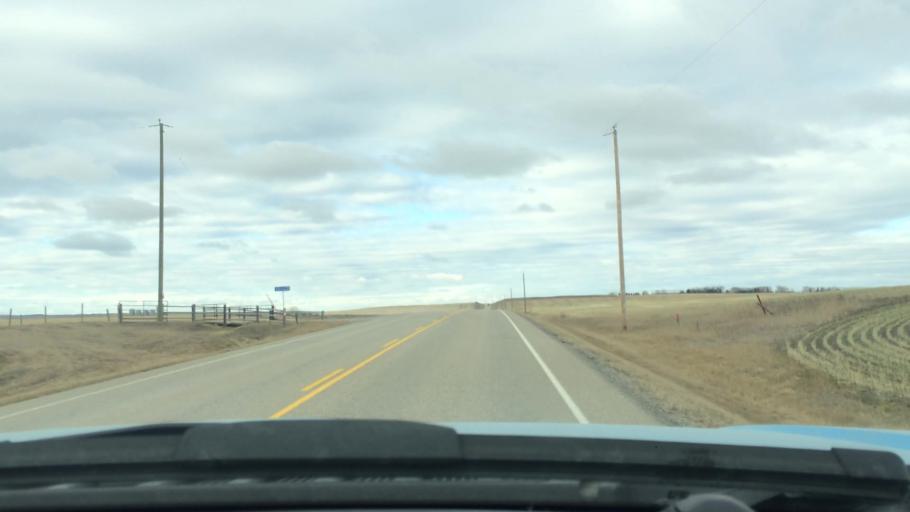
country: CA
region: Alberta
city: Airdrie
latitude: 51.2124
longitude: -114.1054
